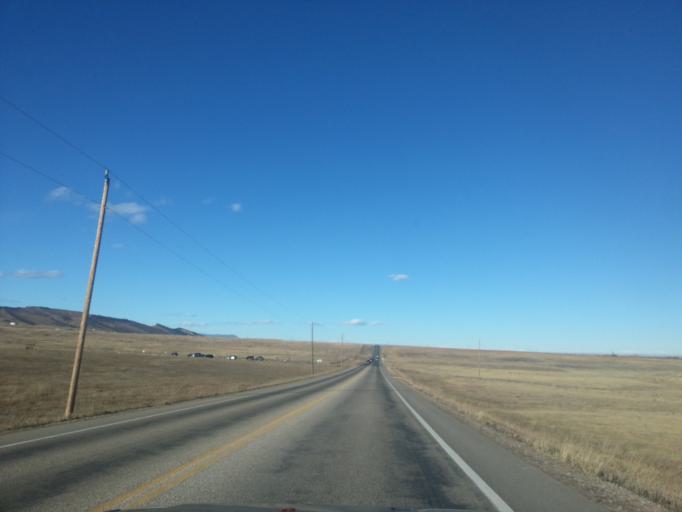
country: US
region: Colorado
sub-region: Larimer County
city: Loveland
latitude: 40.4780
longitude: -105.1157
